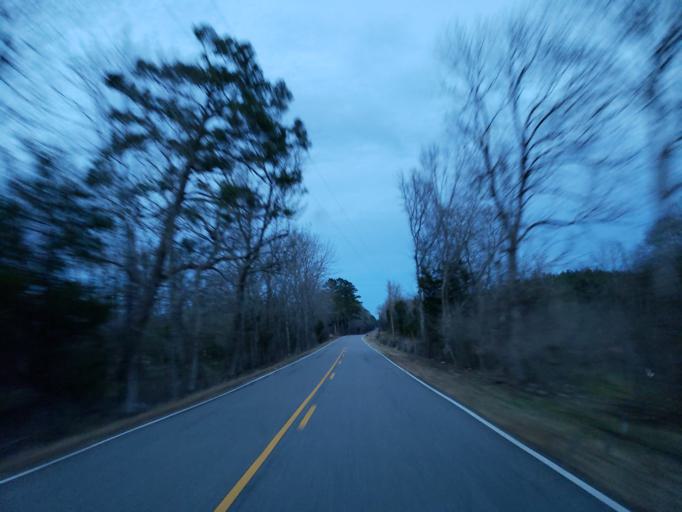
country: US
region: Alabama
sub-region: Greene County
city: Eutaw
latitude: 32.8804
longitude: -88.0702
